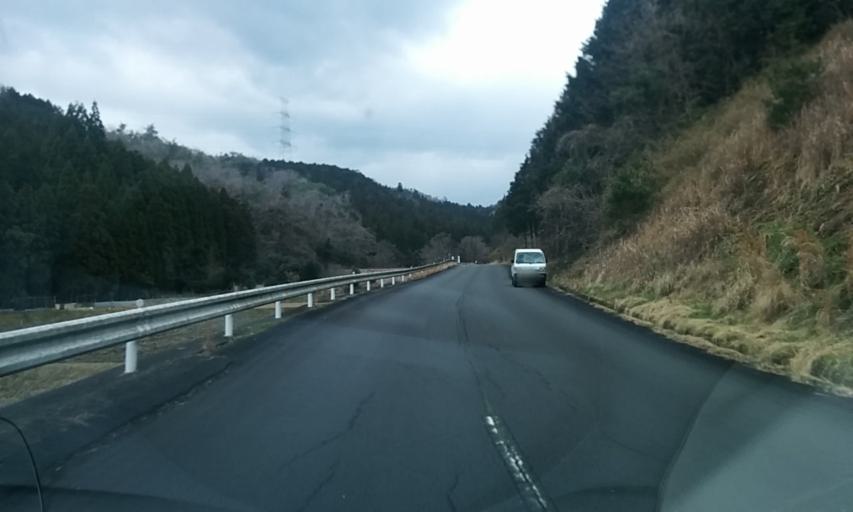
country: JP
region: Kyoto
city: Kameoka
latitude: 35.1094
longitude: 135.4391
